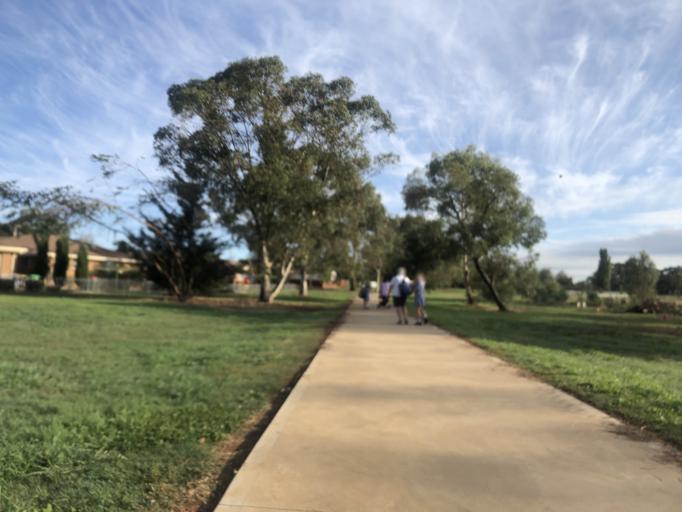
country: AU
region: New South Wales
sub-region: Orange Municipality
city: Orange
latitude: -33.2962
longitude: 149.0917
